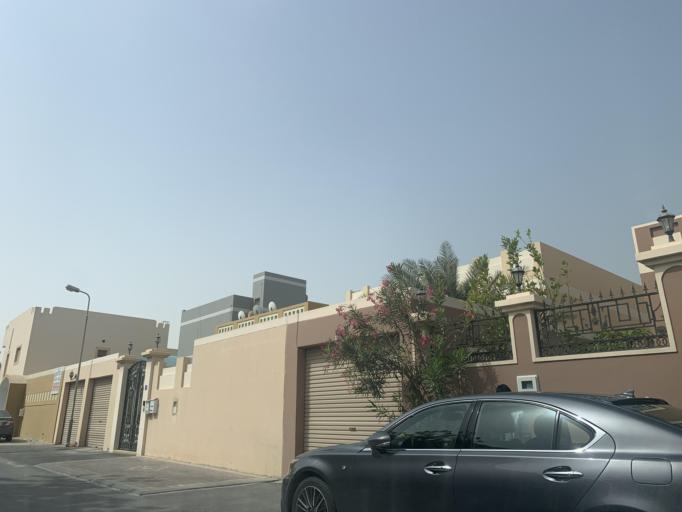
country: BH
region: Northern
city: Ar Rifa'
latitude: 26.1300
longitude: 50.5665
